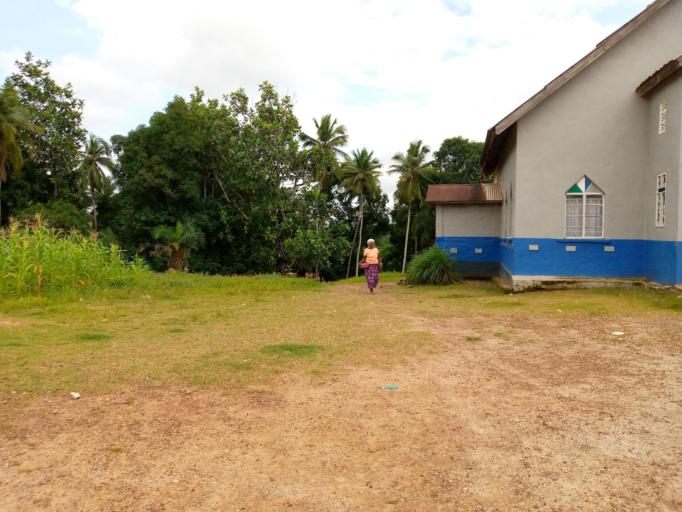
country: SL
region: Northern Province
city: Magburaka
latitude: 8.7219
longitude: -11.9535
